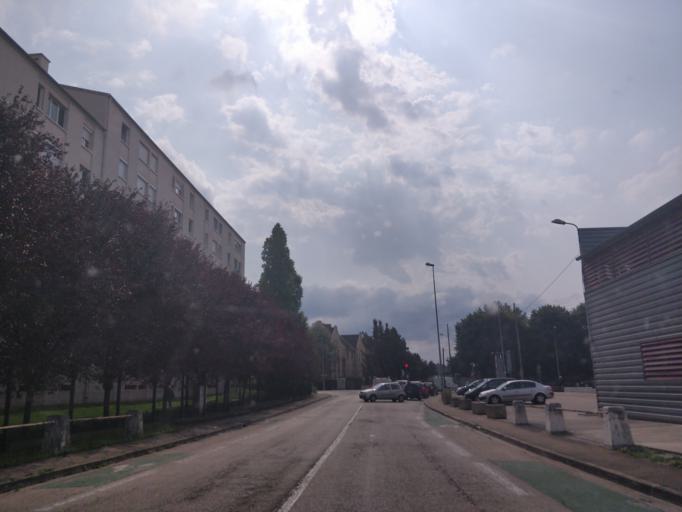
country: FR
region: Champagne-Ardenne
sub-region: Departement de l'Aube
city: Saint-Julien-les-Villas
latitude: 48.2777
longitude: 4.0836
